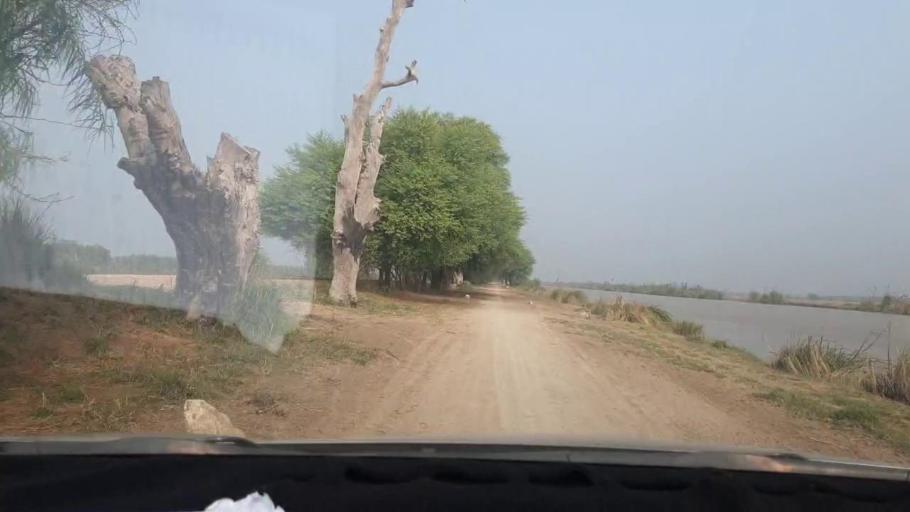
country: PK
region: Sindh
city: Tando Adam
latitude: 25.6755
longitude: 68.5575
